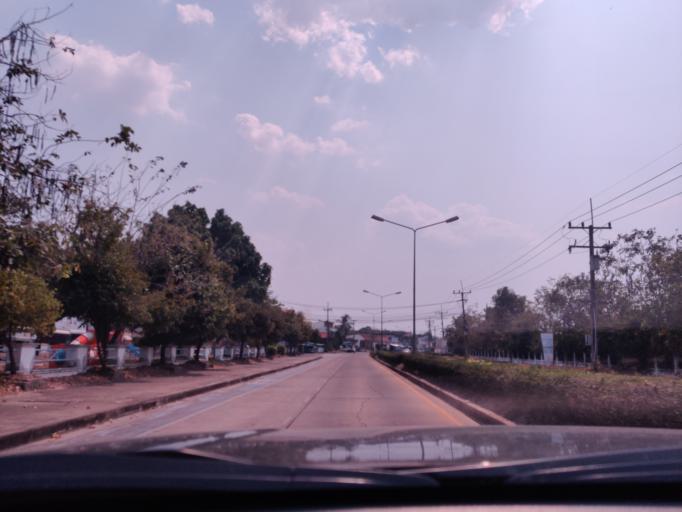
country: TH
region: Sisaket
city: Si Sa Ket
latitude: 15.1016
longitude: 104.3148
